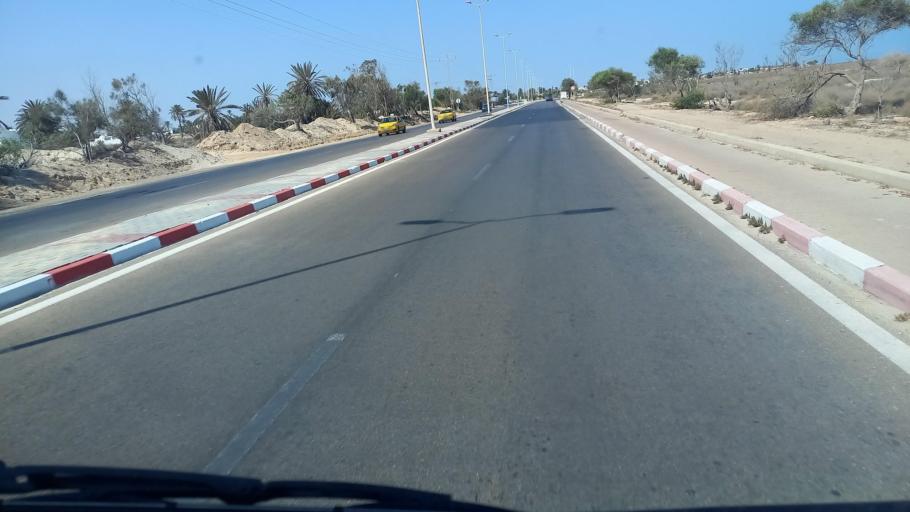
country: TN
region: Madanin
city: Midoun
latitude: 33.8690
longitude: 10.9484
